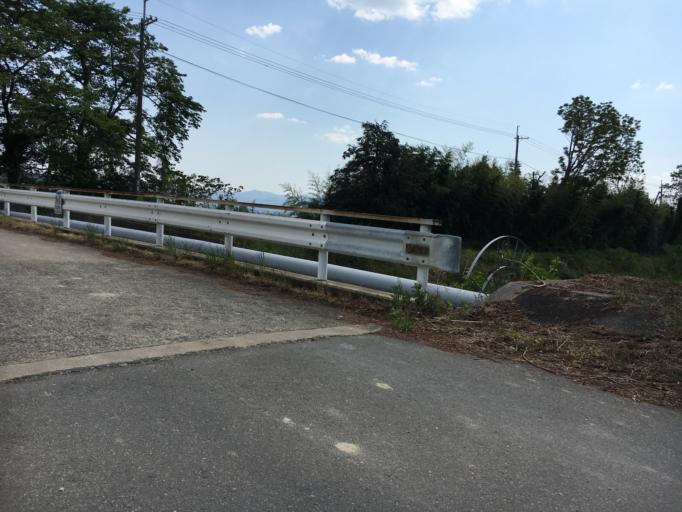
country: JP
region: Kyoto
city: Kameoka
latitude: 35.0833
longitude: 135.5556
